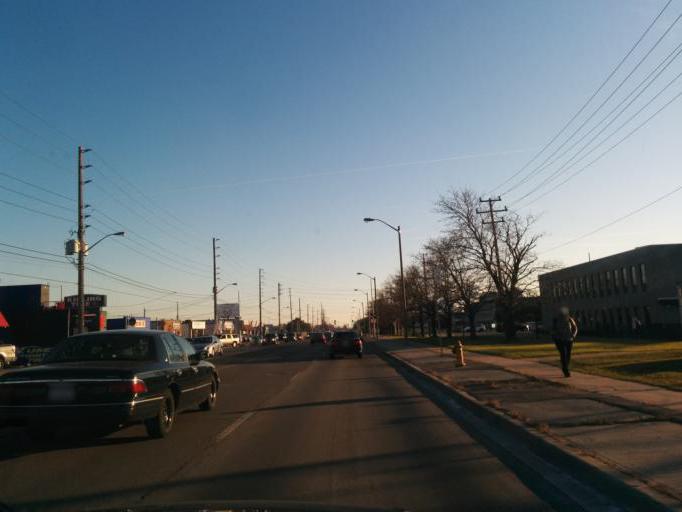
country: CA
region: Ontario
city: Etobicoke
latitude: 43.6335
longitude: -79.5320
